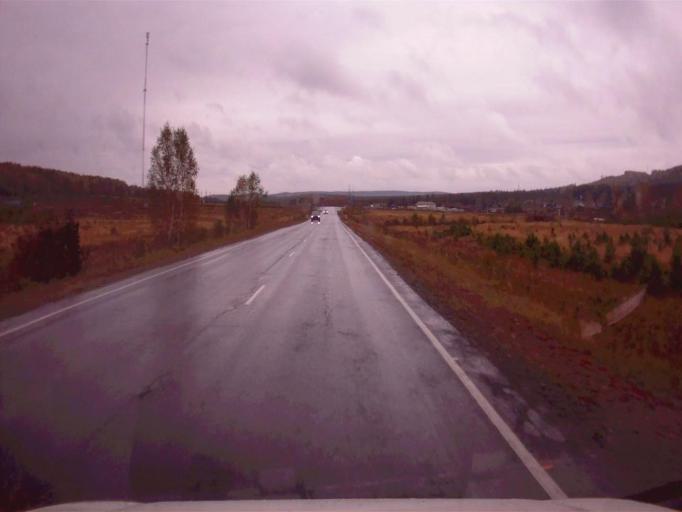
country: RU
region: Chelyabinsk
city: Verkhniy Ufaley
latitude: 55.9994
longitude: 60.3306
